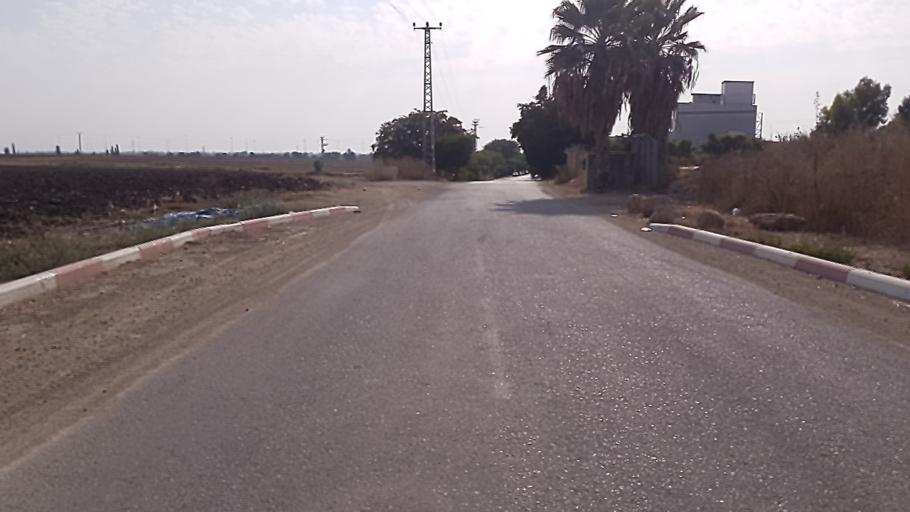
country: IL
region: Central District
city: Rosh Ha'Ayin
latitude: 32.0806
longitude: 34.9423
